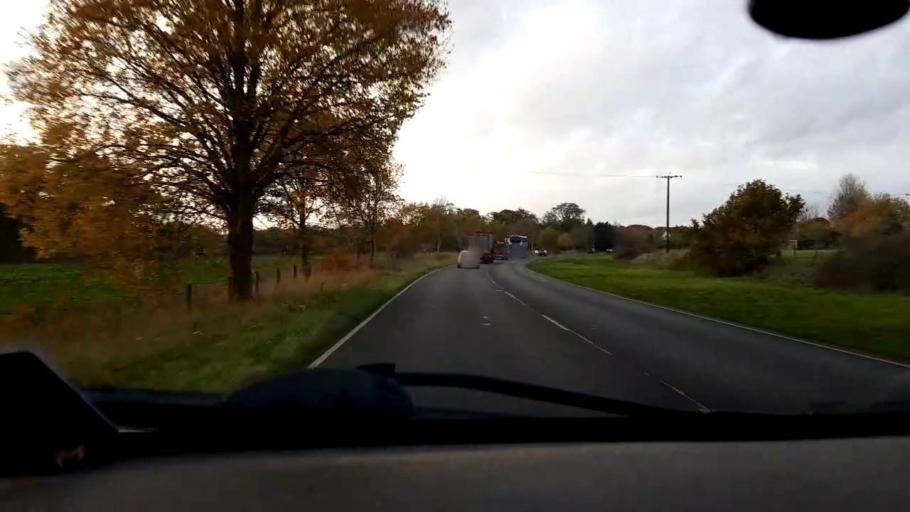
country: GB
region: England
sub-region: Norfolk
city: Costessey
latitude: 52.7072
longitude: 1.1458
